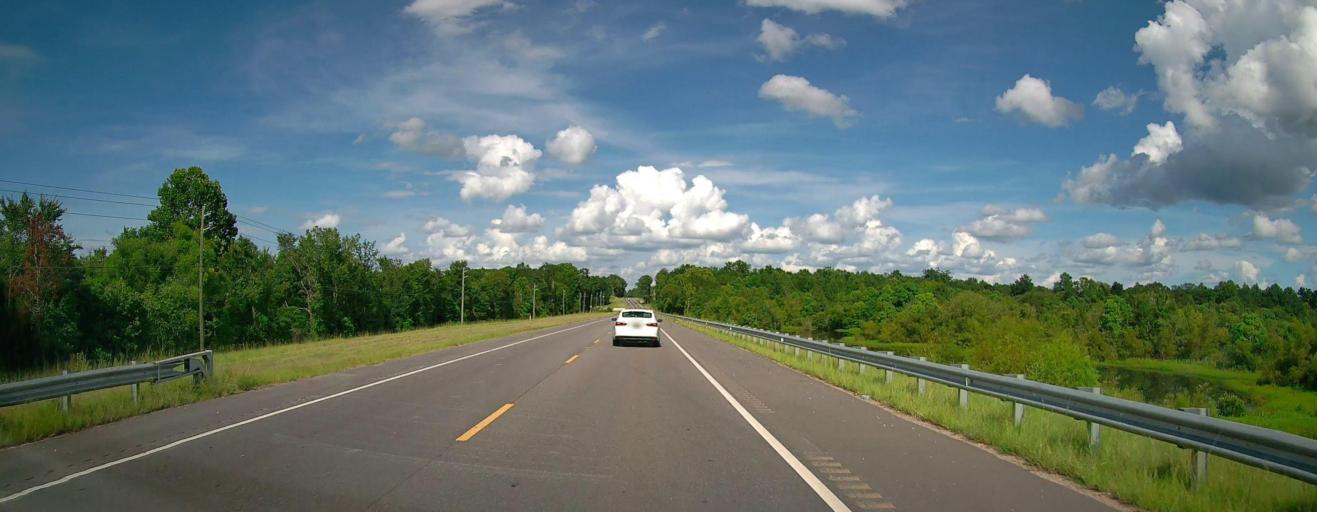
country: US
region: Alabama
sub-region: Russell County
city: Ladonia
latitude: 32.4610
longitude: -85.1367
